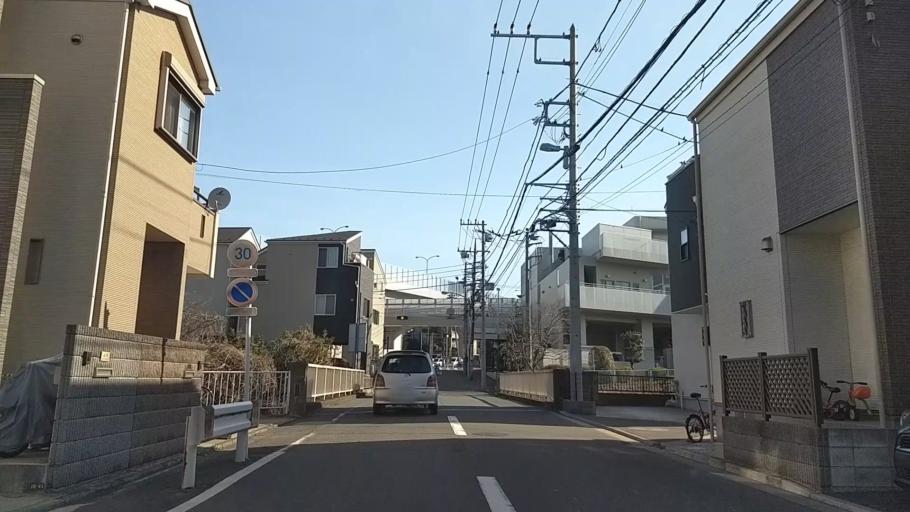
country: JP
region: Kanagawa
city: Yokohama
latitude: 35.3920
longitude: 139.5995
